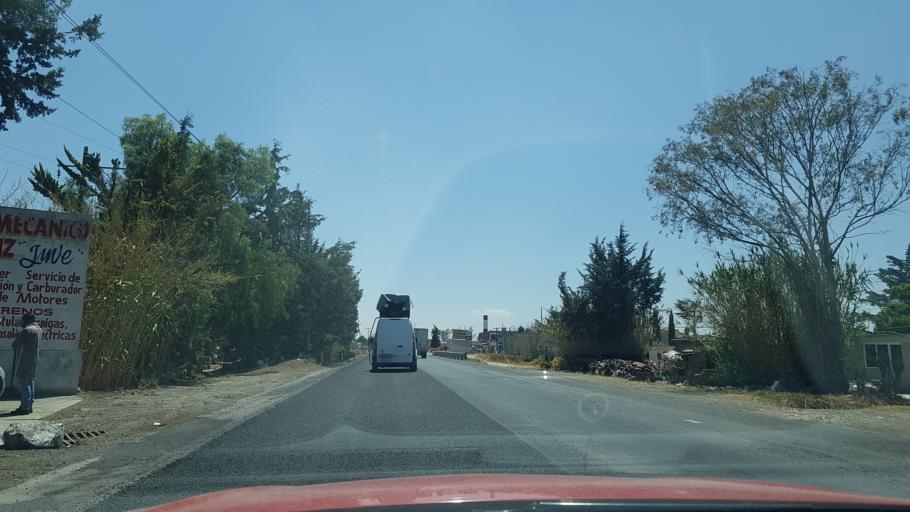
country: MX
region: Mexico
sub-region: Ixtlahuaca
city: Santo Domingo de Guzman
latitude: 19.5956
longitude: -99.7721
